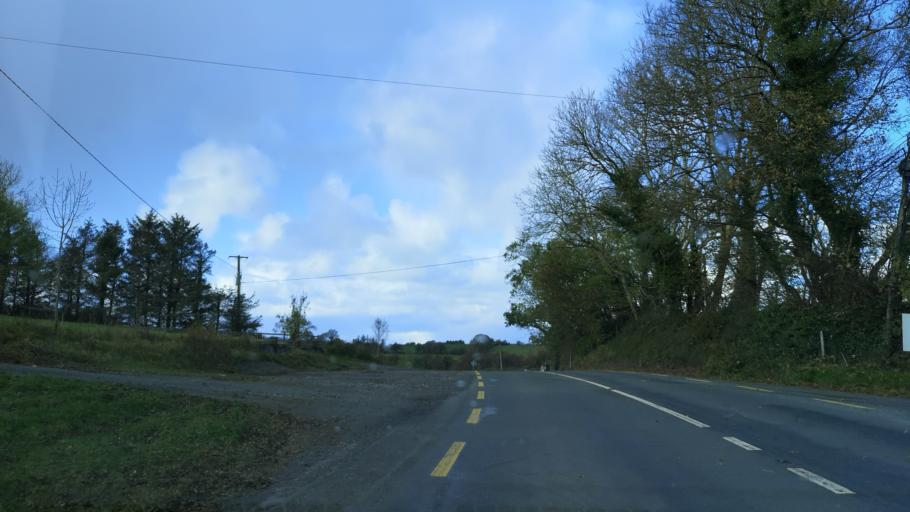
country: IE
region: Connaught
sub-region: Maigh Eo
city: Westport
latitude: 53.7764
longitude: -9.4036
